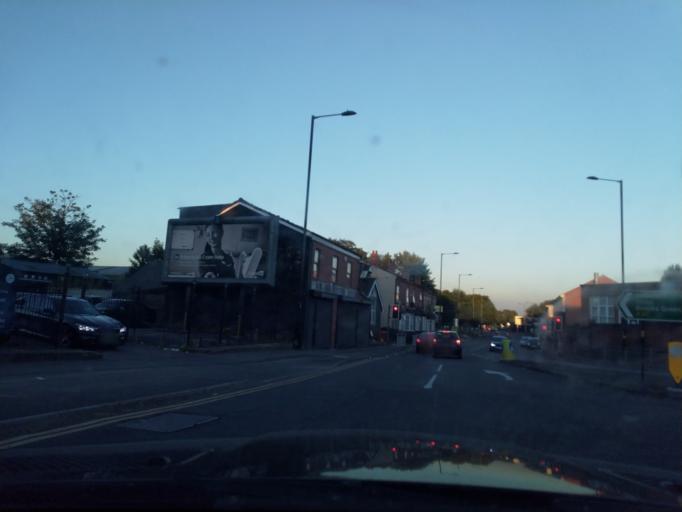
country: GB
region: England
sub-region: City and Borough of Birmingham
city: Acocks Green
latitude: 52.4550
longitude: -1.8582
